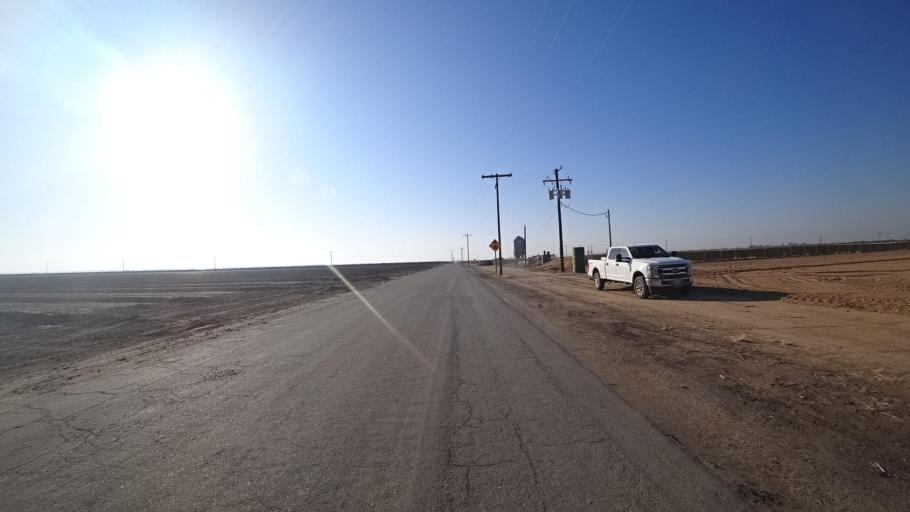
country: US
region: California
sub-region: Tulare County
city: Richgrove
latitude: 35.7639
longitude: -119.1519
